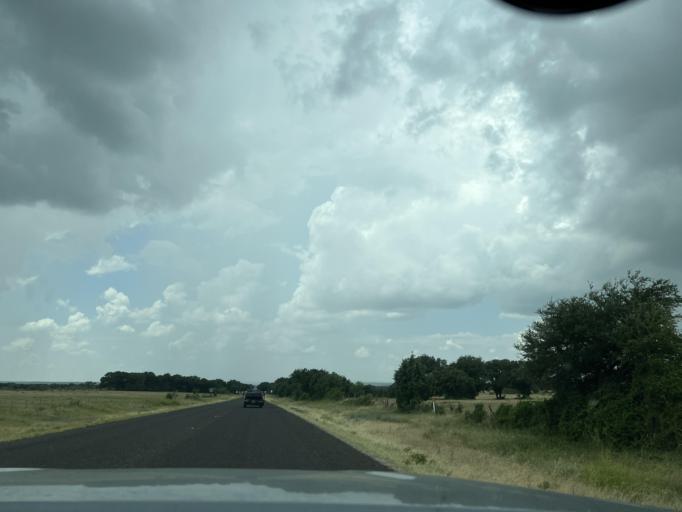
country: US
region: Texas
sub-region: Wise County
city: Decatur
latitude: 33.1632
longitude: -97.6284
